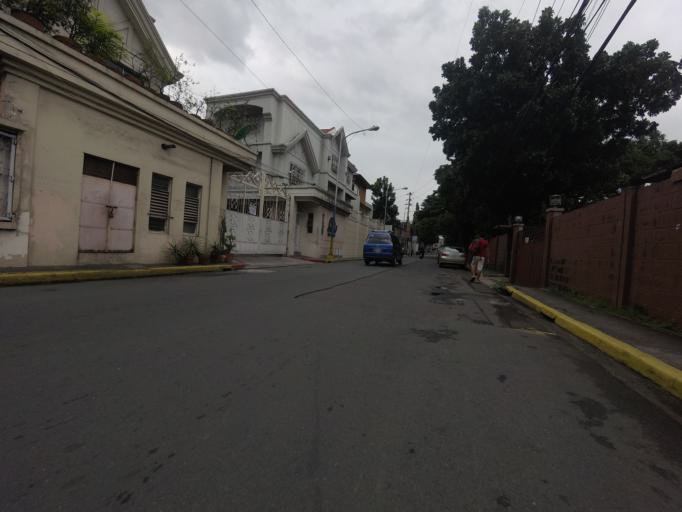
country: PH
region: Metro Manila
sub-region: Mandaluyong
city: Mandaluyong City
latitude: 14.5916
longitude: 121.0418
